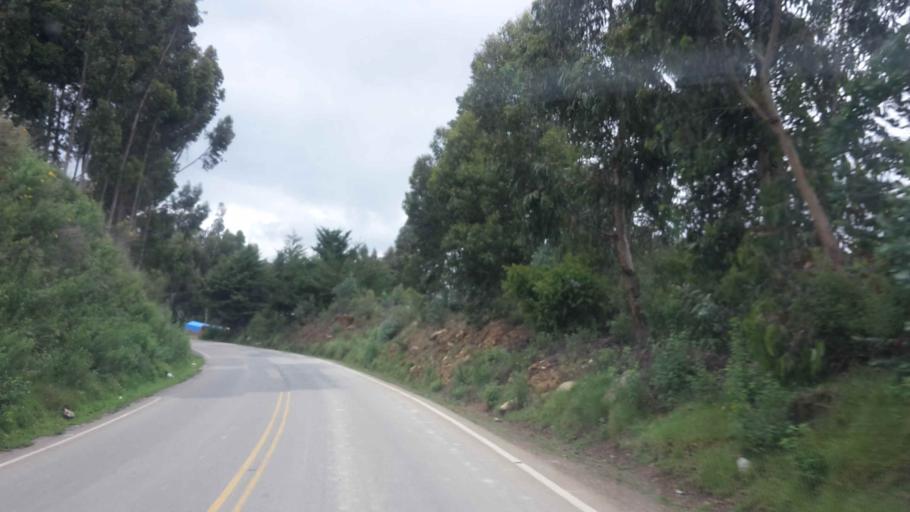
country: BO
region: Cochabamba
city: Totora
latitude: -17.5727
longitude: -65.3170
